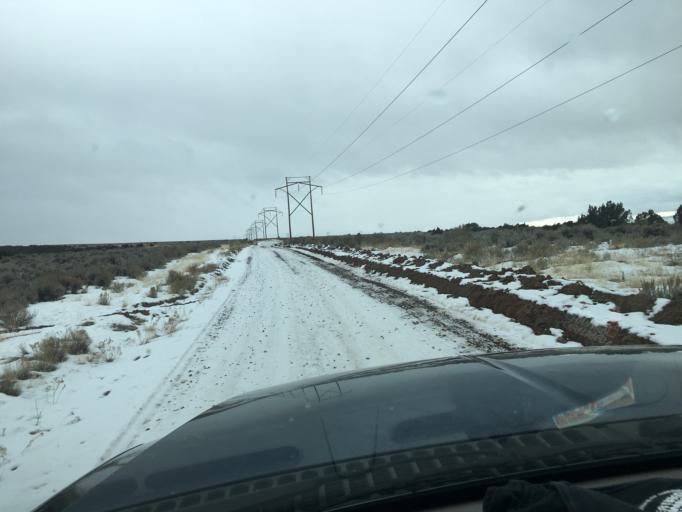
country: US
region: Colorado
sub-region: Garfield County
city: Parachute
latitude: 39.3445
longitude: -108.1695
